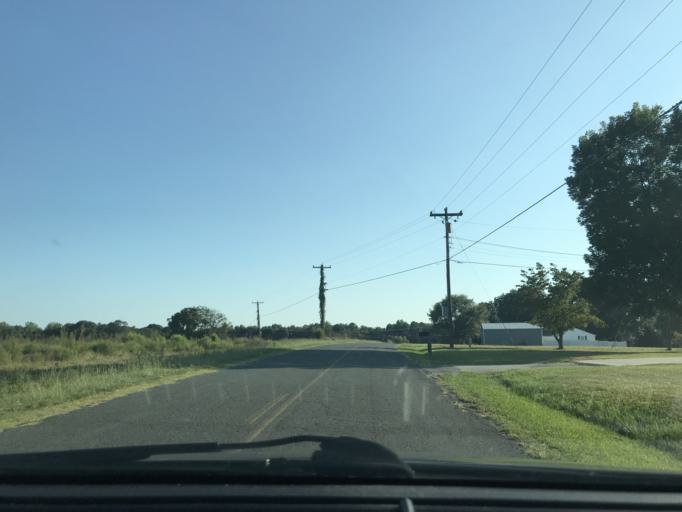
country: US
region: North Carolina
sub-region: Cleveland County
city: Boiling Springs
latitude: 35.1655
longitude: -81.7329
